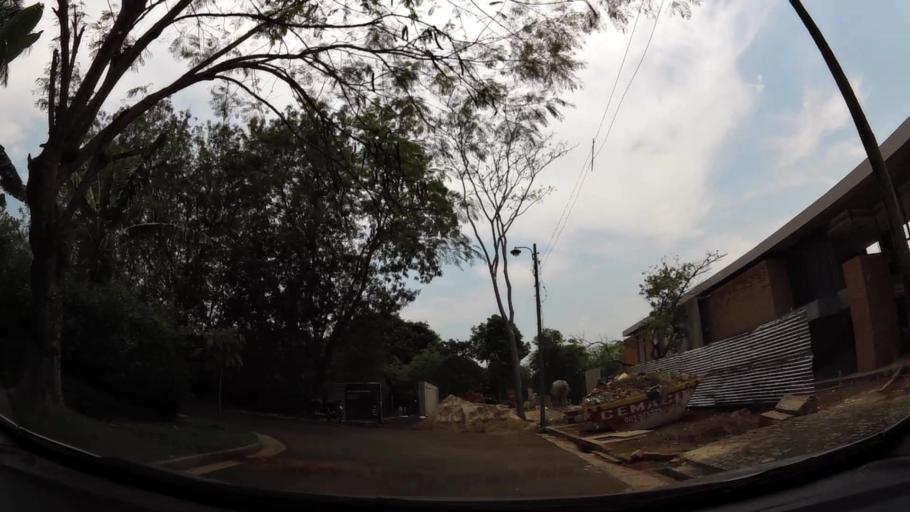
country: PY
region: Alto Parana
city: Ciudad del Este
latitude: -25.4879
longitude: -54.6120
